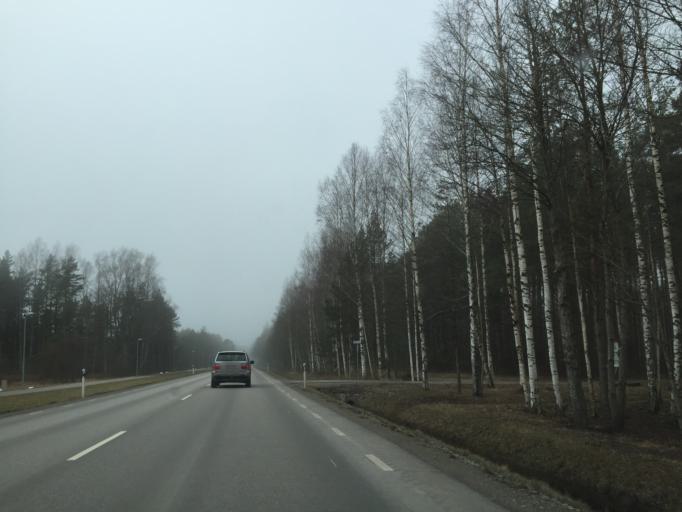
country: EE
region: Saare
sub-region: Kuressaare linn
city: Kuressaare
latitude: 58.2209
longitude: 22.3497
